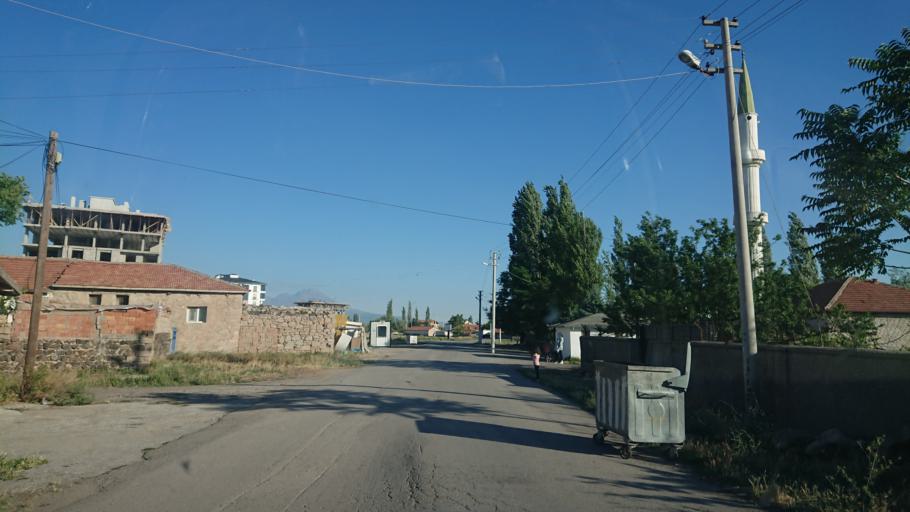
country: TR
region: Aksaray
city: Aksaray
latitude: 38.3841
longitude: 33.9909
